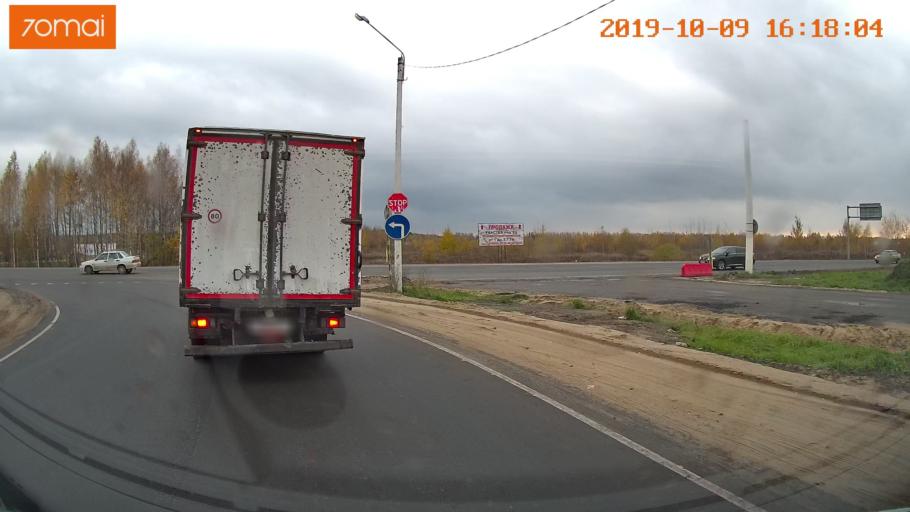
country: RU
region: Kostroma
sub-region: Kostromskoy Rayon
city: Kostroma
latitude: 57.7269
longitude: 40.8946
